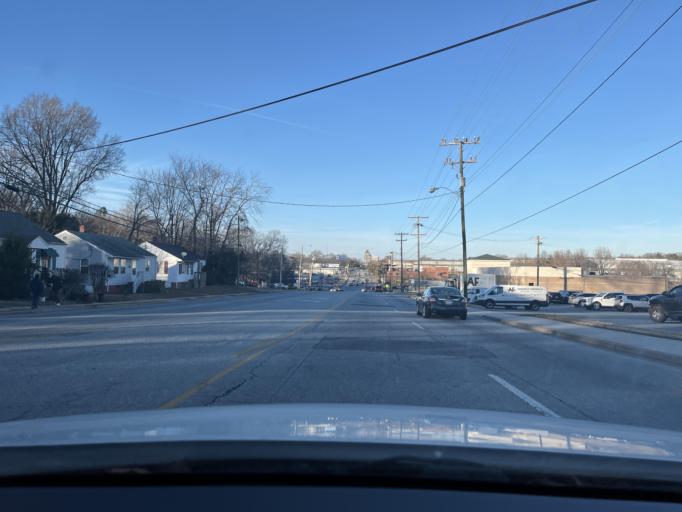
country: US
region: North Carolina
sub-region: Guilford County
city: Greensboro
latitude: 36.0461
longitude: -79.7915
